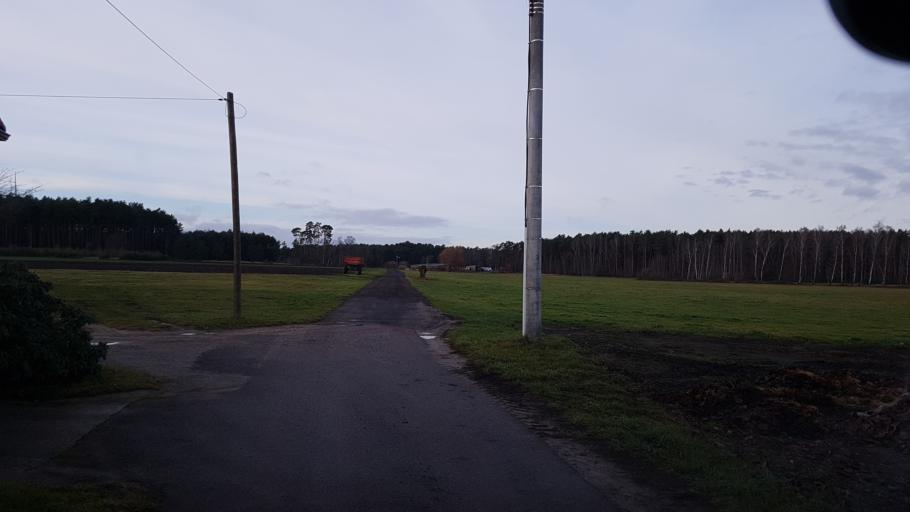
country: DE
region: Brandenburg
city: Sallgast
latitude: 51.6436
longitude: 13.8496
